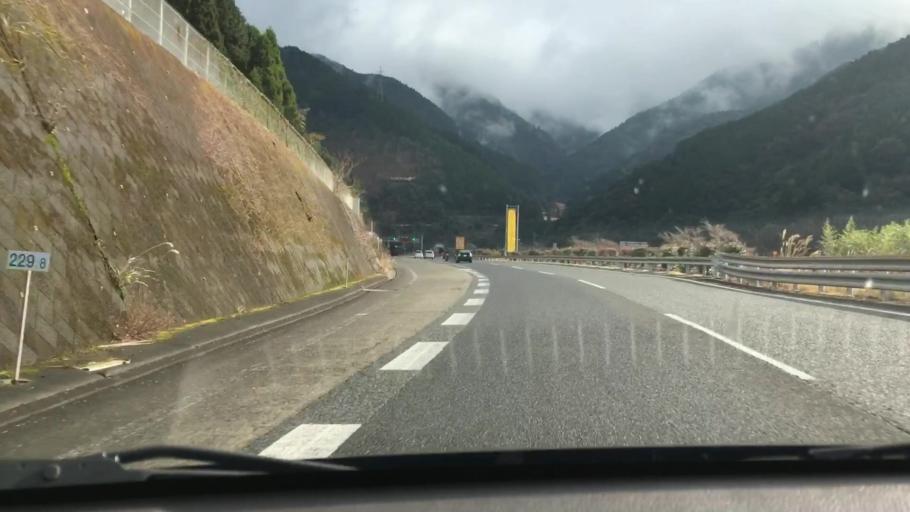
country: JP
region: Kumamoto
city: Yatsushiro
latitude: 32.3979
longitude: 130.7030
